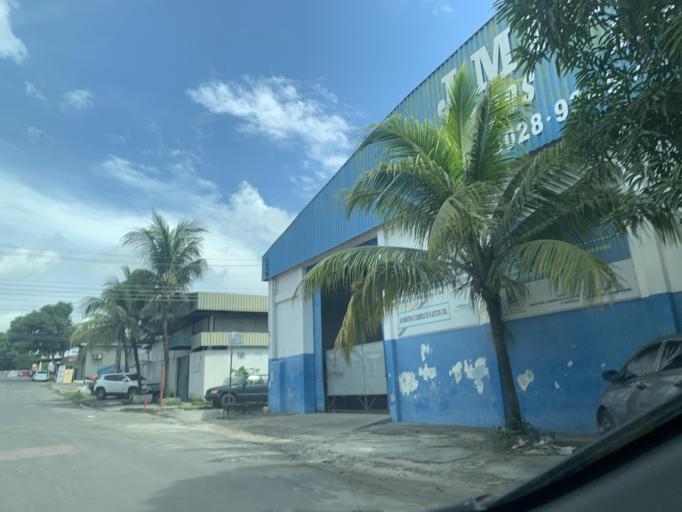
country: BR
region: Amazonas
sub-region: Manaus
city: Manaus
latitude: -3.0930
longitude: -59.9514
